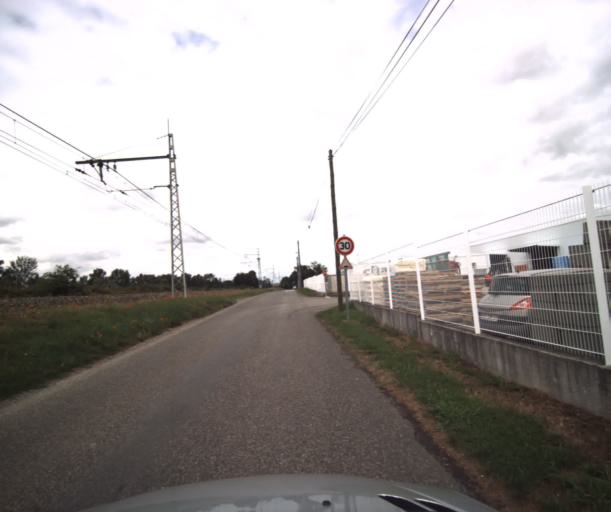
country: FR
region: Midi-Pyrenees
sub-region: Departement de la Haute-Garonne
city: Lacroix-Falgarde
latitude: 43.4897
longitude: 1.3947
